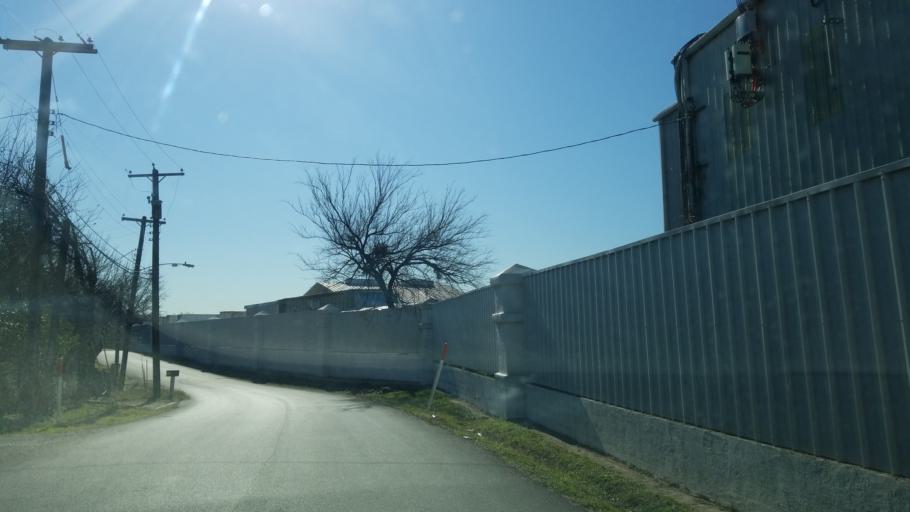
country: US
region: Texas
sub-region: Dallas County
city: Cockrell Hill
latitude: 32.7572
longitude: -96.9167
